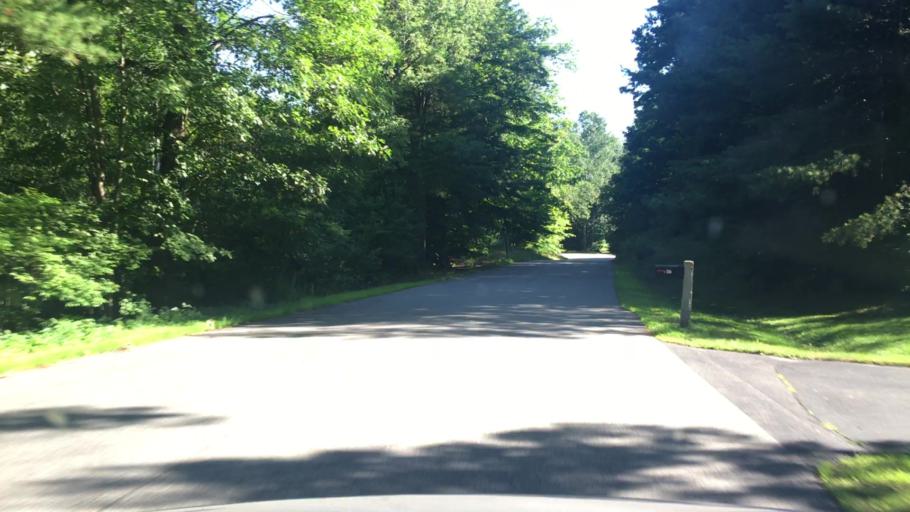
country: US
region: New Hampshire
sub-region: Rockingham County
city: Exeter
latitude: 43.0340
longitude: -70.9637
